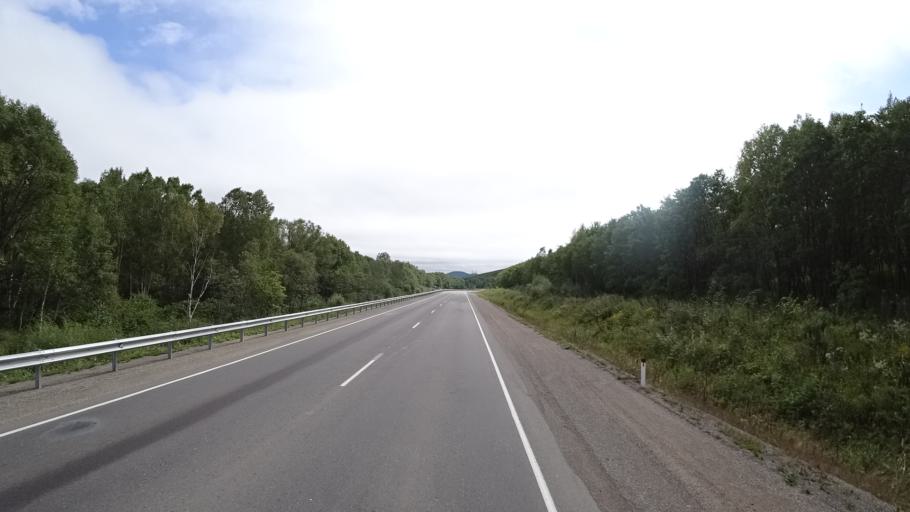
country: RU
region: Primorskiy
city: Lyalichi
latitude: 44.1141
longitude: 132.4195
